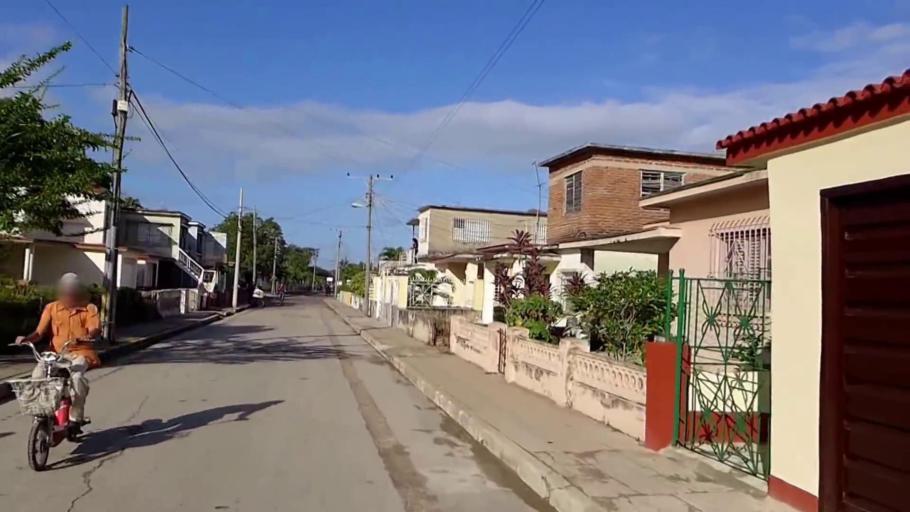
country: CU
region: Camaguey
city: Camaguey
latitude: 21.3873
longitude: -77.9236
